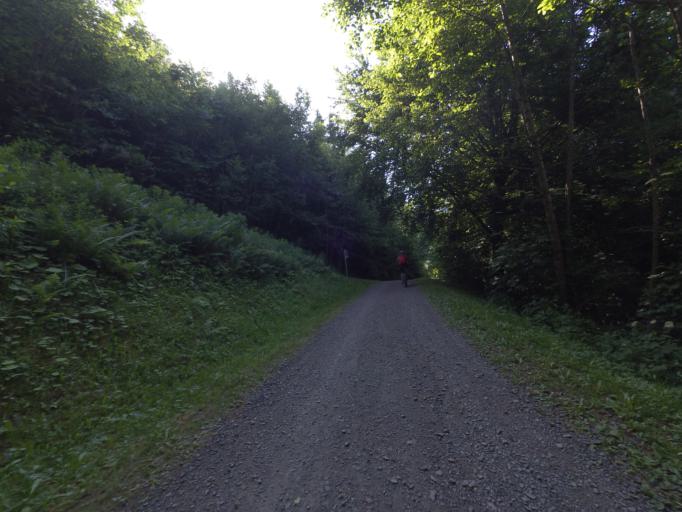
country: AT
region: Carinthia
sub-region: Politischer Bezirk Spittal an der Drau
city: Millstatt
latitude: 46.7995
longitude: 13.5512
